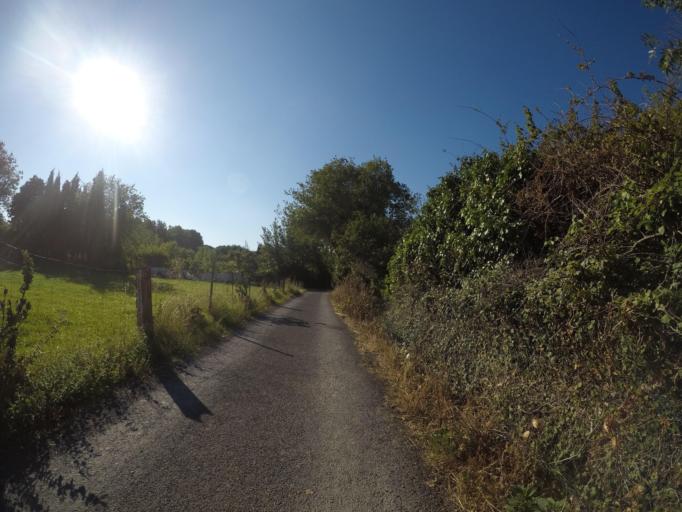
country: FR
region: Languedoc-Roussillon
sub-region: Departement des Pyrenees-Orientales
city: Pezilla-la-Riviere
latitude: 42.6812
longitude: 2.7531
